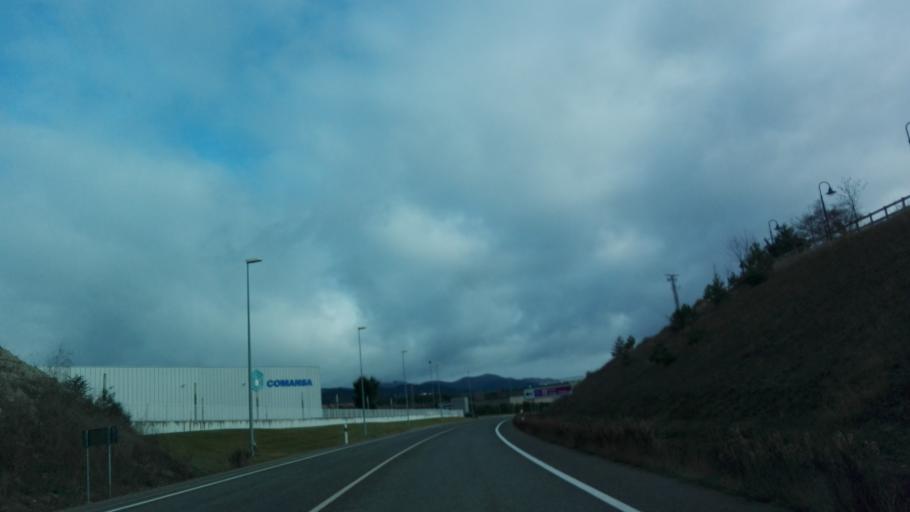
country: ES
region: Navarre
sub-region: Provincia de Navarra
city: Egues-Uharte
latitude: 42.8292
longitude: -1.5788
